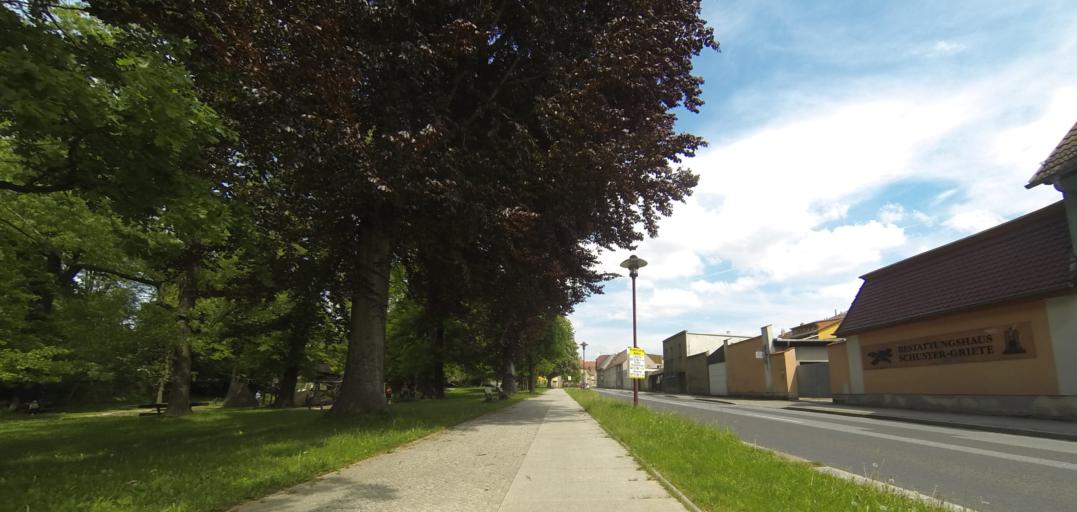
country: DE
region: Saxony
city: Bischofswerda
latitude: 51.1279
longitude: 14.1766
